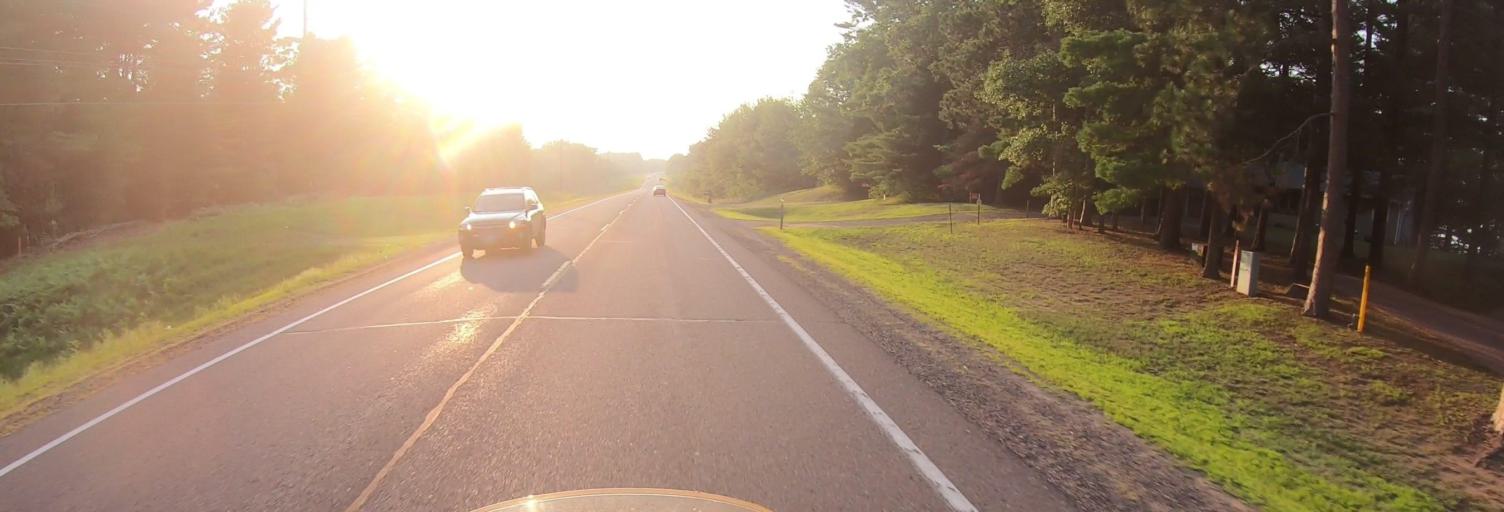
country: US
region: Wisconsin
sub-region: Burnett County
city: Siren
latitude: 45.8116
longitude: -92.2261
